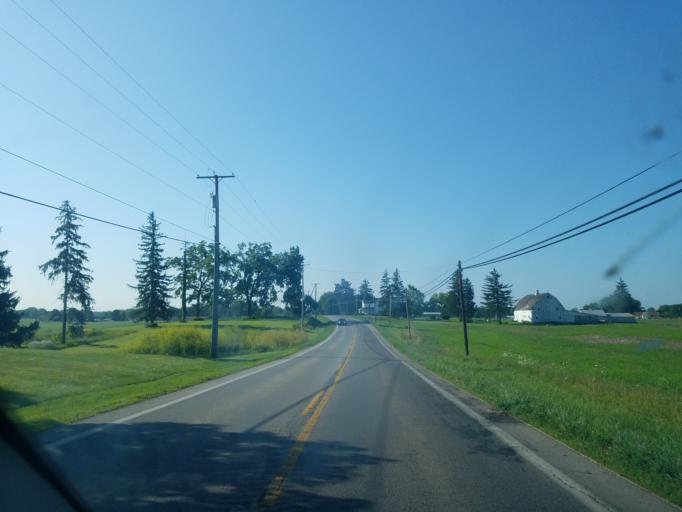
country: US
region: Ohio
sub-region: Marion County
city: Marion
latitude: 40.5396
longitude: -83.1095
